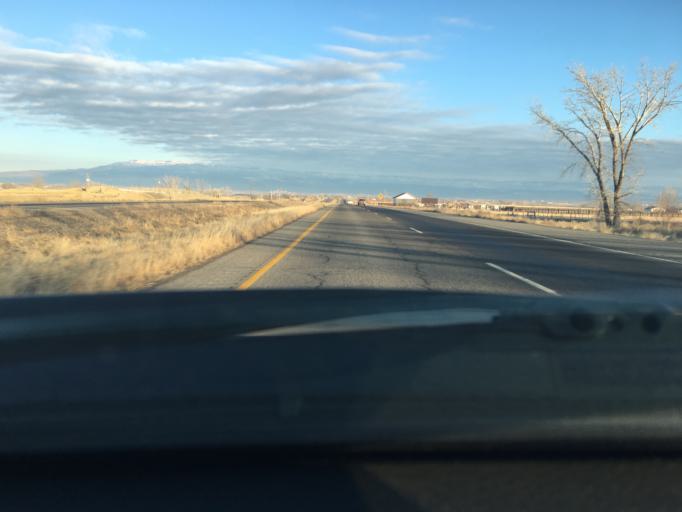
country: US
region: Colorado
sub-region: Montrose County
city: Olathe
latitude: 38.6314
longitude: -107.9857
